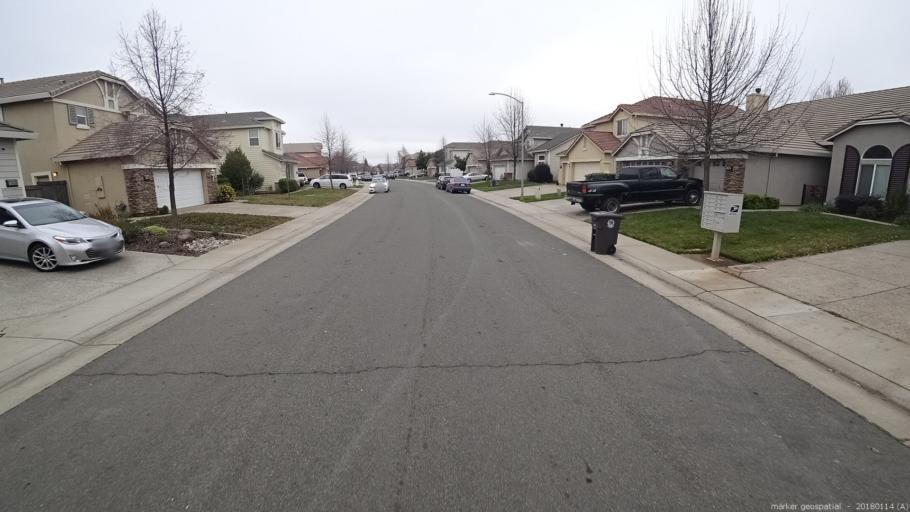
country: US
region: California
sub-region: Sacramento County
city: Rancho Cordova
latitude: 38.5461
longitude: -121.2358
